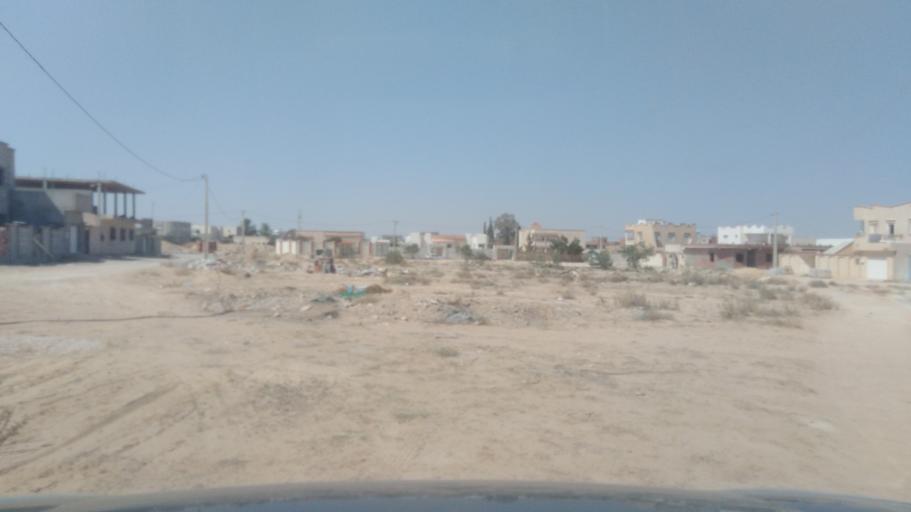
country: TN
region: Qabis
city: Gabes
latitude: 33.9552
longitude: 10.0167
